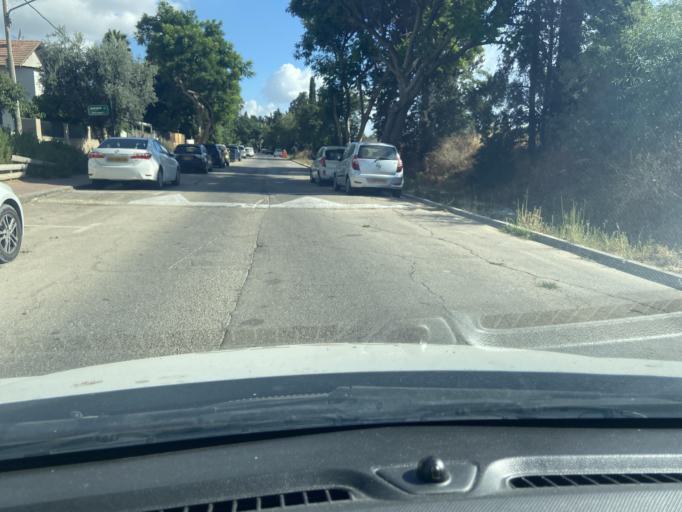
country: IL
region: Central District
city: Yehud
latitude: 32.0355
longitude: 34.8989
